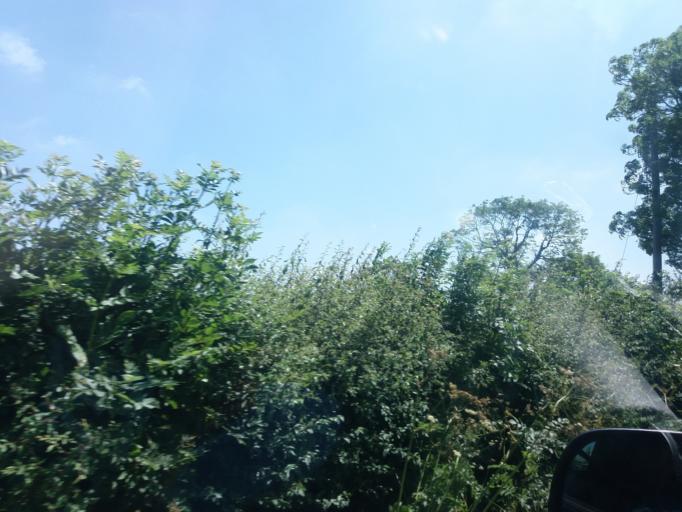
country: IE
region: Leinster
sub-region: Fingal County
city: Swords
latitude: 53.5321
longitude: -6.2507
